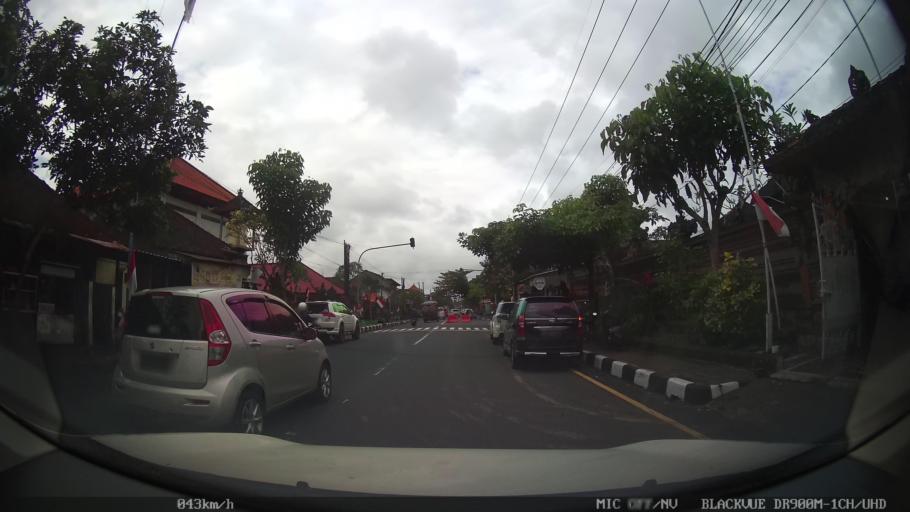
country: ID
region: Bali
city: Banjar Serangan
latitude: -8.5478
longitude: 115.1698
